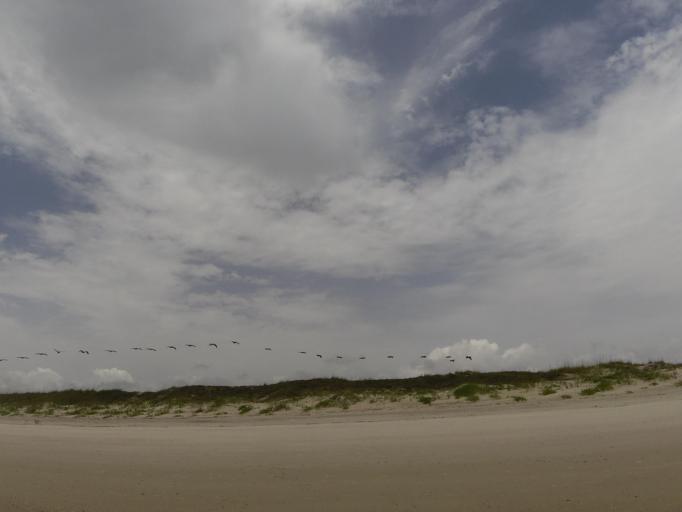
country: US
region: Florida
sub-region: Saint Johns County
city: Saint Augustine Beach
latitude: 29.8854
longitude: -81.2732
